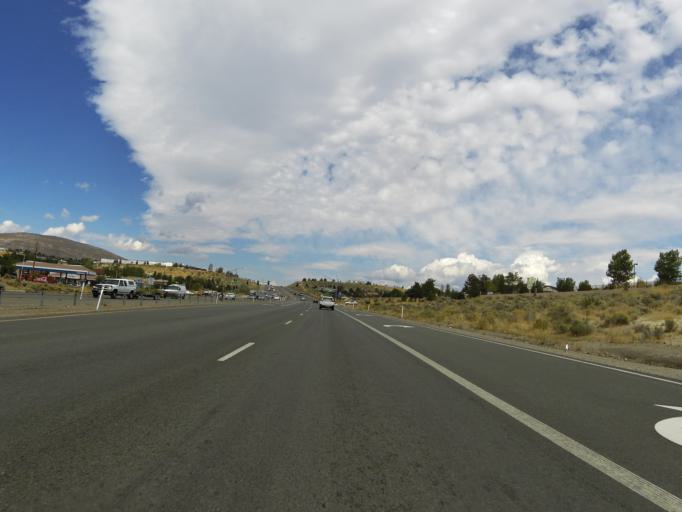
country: US
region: Nevada
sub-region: Douglas County
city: Indian Hills
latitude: 39.0897
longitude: -119.7756
